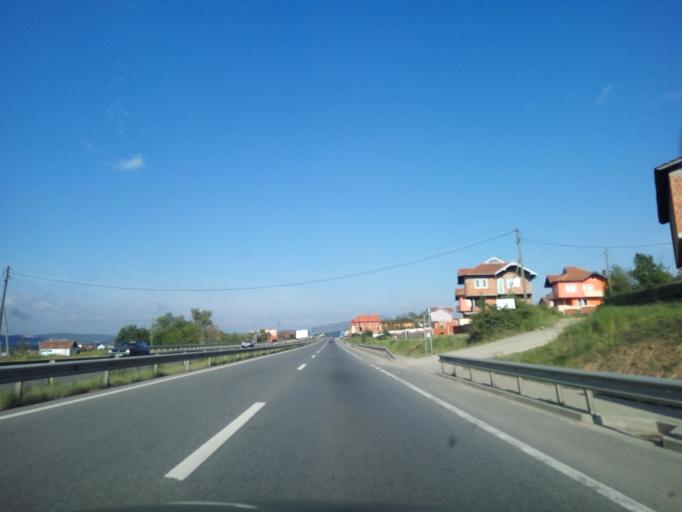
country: XK
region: Pristina
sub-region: Komuna e Drenasit
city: Glogovac
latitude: 42.5762
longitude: 20.8621
